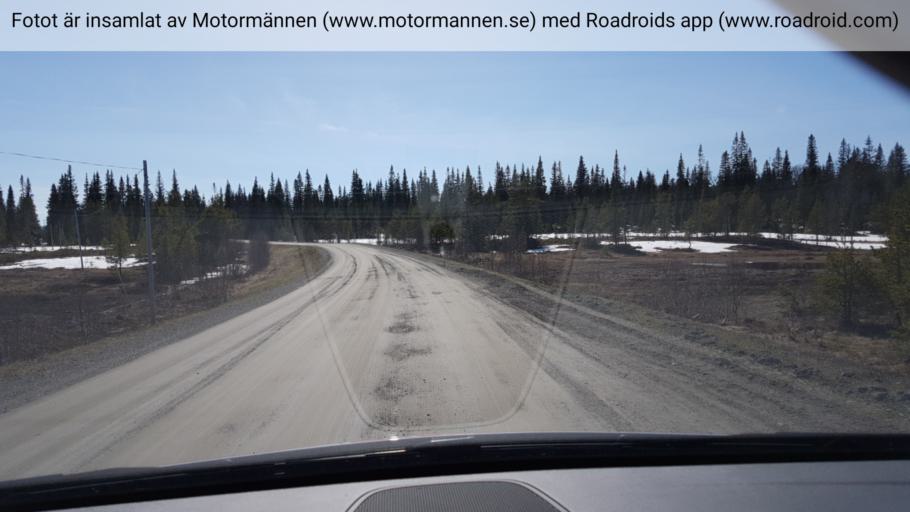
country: NO
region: Nord-Trondelag
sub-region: Snasa
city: Snaase
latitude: 63.7383
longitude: 12.4700
